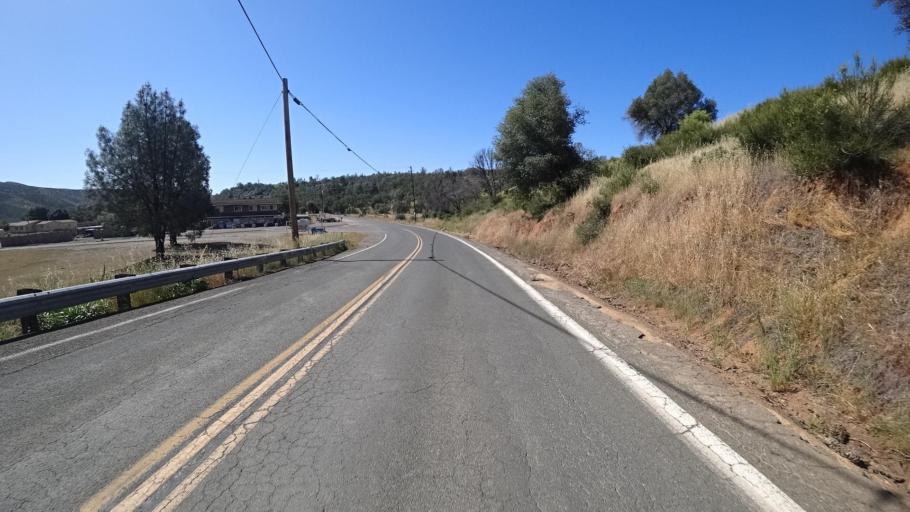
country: US
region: California
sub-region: Lake County
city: Clearlake Oaks
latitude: 39.0559
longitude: -122.5879
